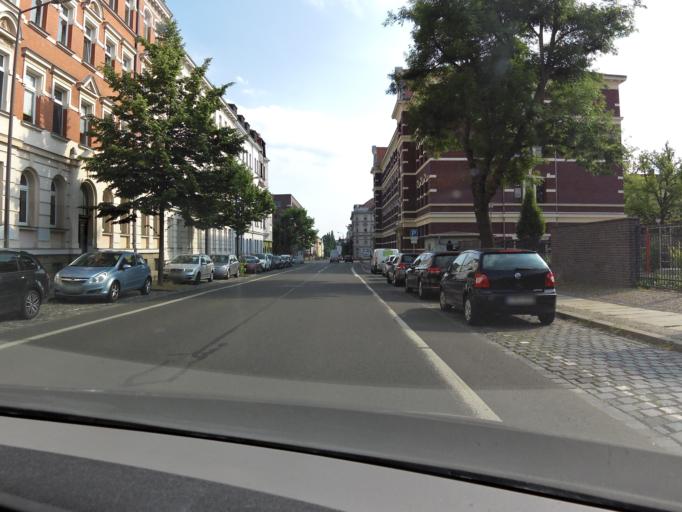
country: DE
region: Saxony
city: Leipzig
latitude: 51.3646
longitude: 12.3619
